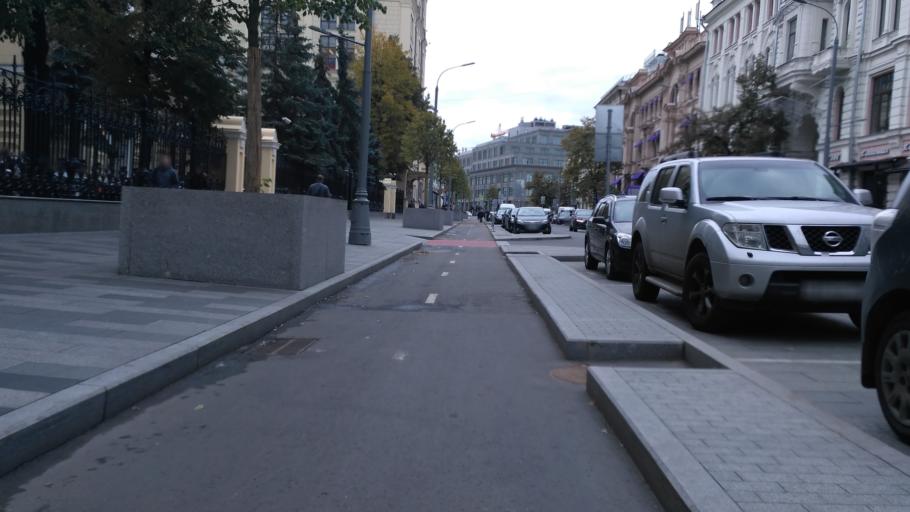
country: RU
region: Moscow
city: Moscow
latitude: 55.7635
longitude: 37.6201
